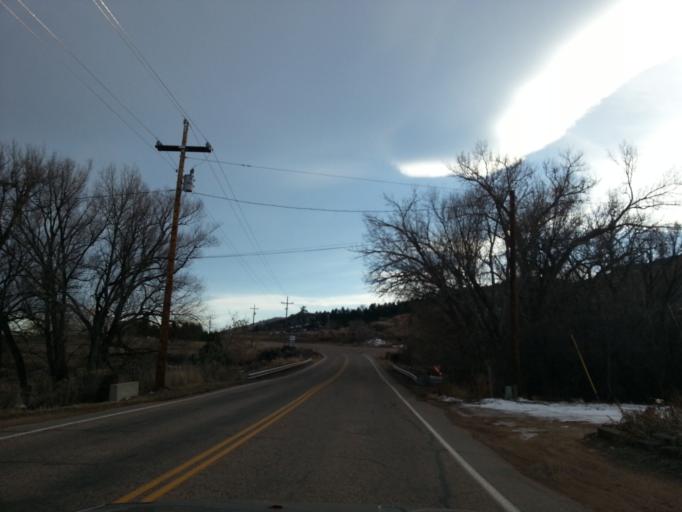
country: US
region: Colorado
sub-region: Larimer County
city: Loveland
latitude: 40.4594
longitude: -105.2067
